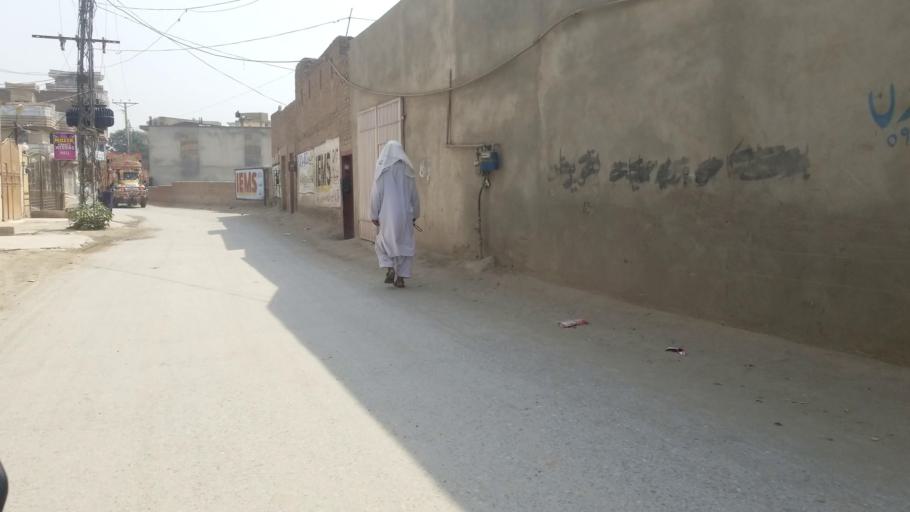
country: PK
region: Khyber Pakhtunkhwa
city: Peshawar
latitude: 33.9830
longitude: 71.5316
